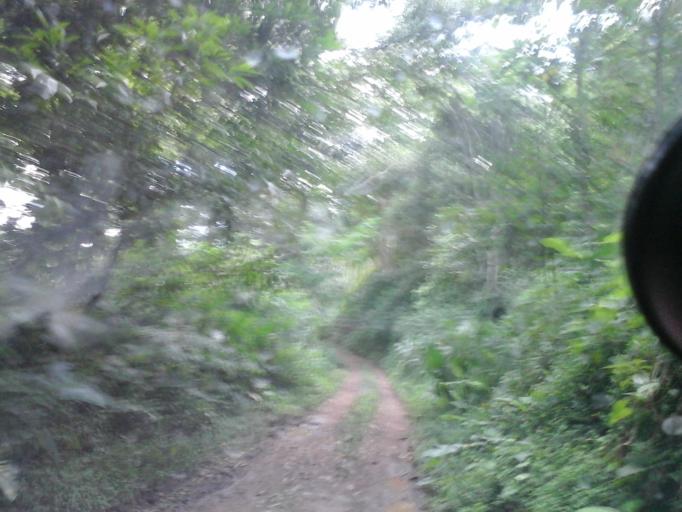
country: CO
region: Cesar
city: San Diego
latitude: 10.2796
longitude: -73.0911
